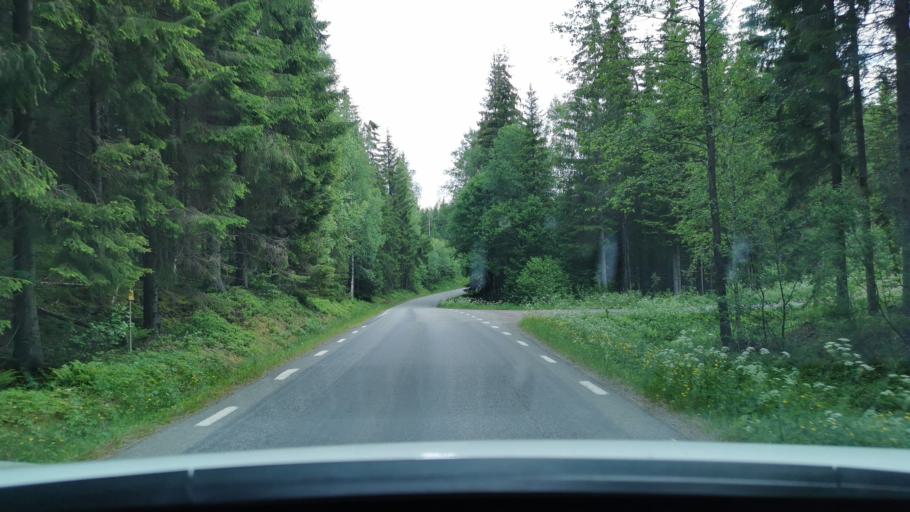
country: SE
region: Vaestra Goetaland
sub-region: Bengtsfors Kommun
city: Dals Langed
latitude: 58.8155
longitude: 12.3265
